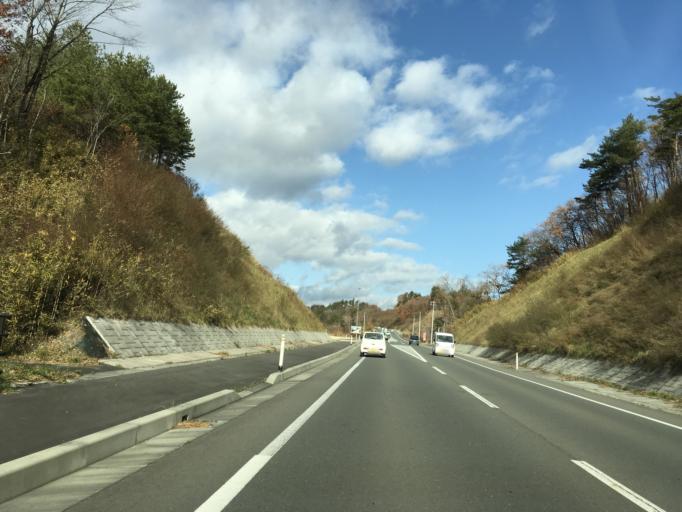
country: JP
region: Iwate
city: Ichinoseki
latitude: 38.8721
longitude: 141.1605
